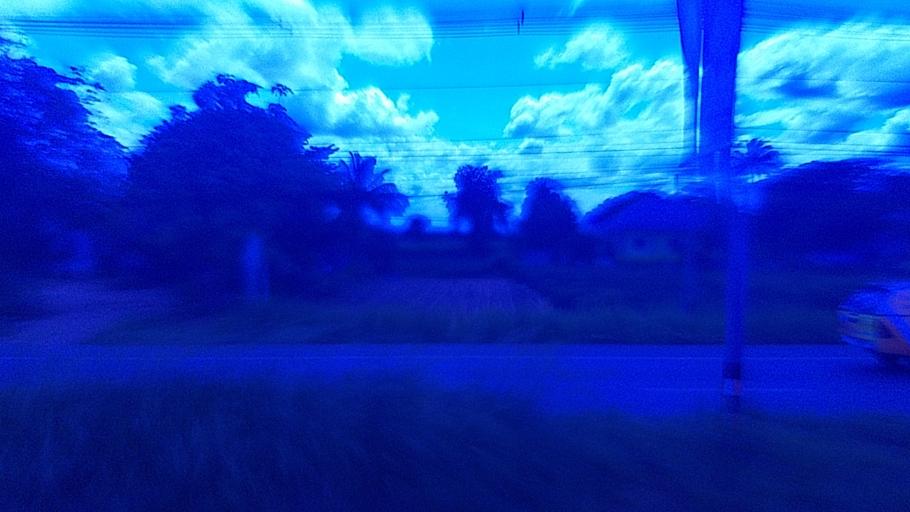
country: TH
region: Nakhon Ratchasima
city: Dan Khun Thot
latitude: 15.1054
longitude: 101.7216
